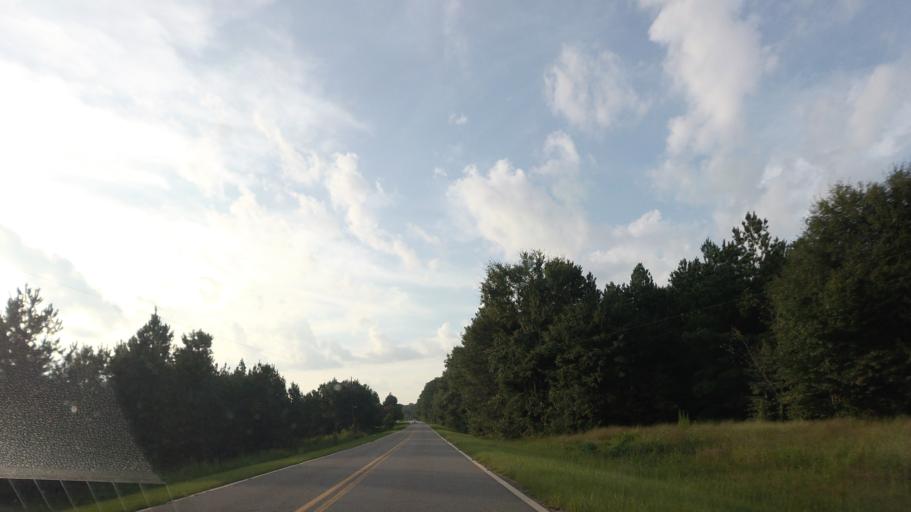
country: US
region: Georgia
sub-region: Wilkinson County
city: Gordon
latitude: 32.8440
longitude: -83.4174
